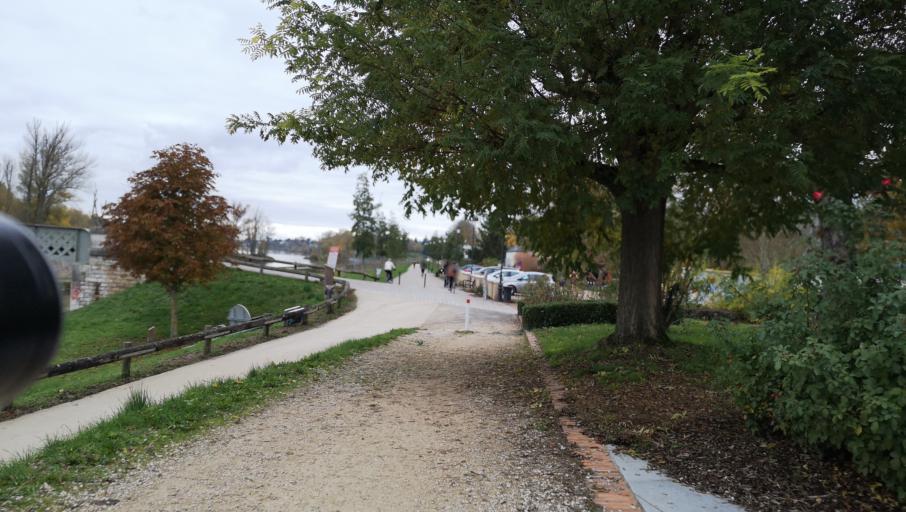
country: FR
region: Centre
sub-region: Departement du Loiret
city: Saint-Jean-de-Braye
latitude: 47.9035
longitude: 1.9633
